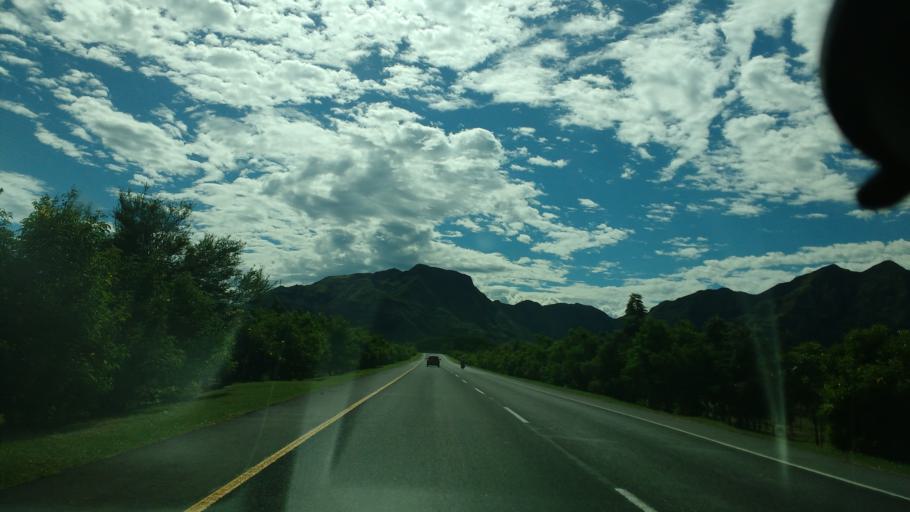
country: CO
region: Tolima
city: Valle de San Juan
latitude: 4.2729
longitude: -75.0012
